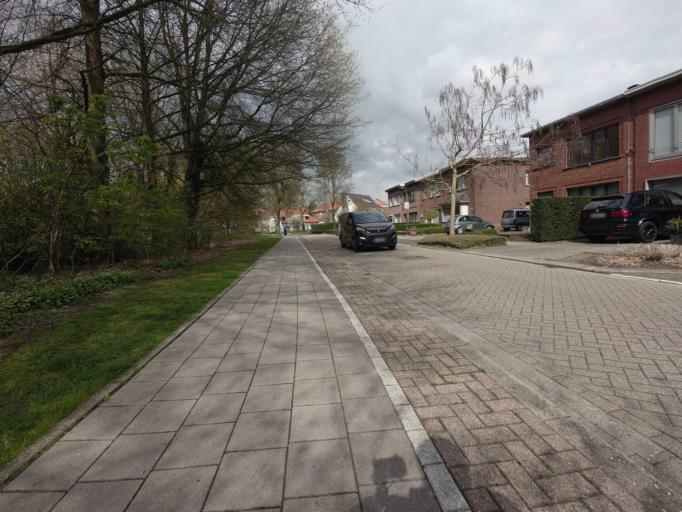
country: BE
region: Flanders
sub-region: Provincie Antwerpen
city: Mortsel
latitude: 51.1731
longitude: 4.4658
